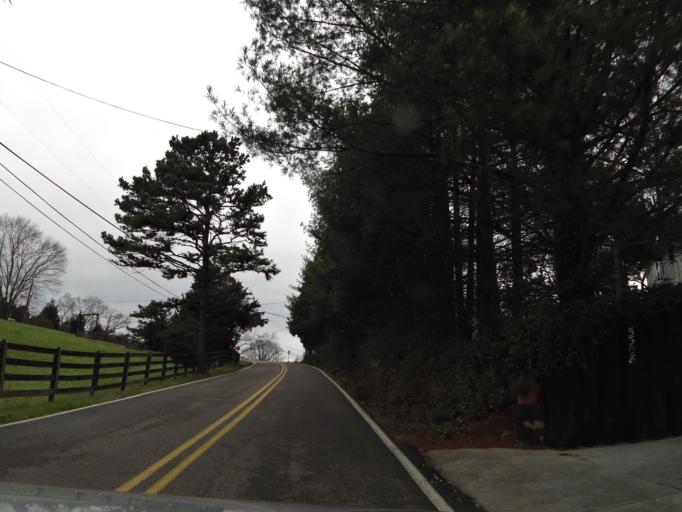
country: US
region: Tennessee
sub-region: Knox County
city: Knoxville
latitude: 35.9889
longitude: -84.0281
